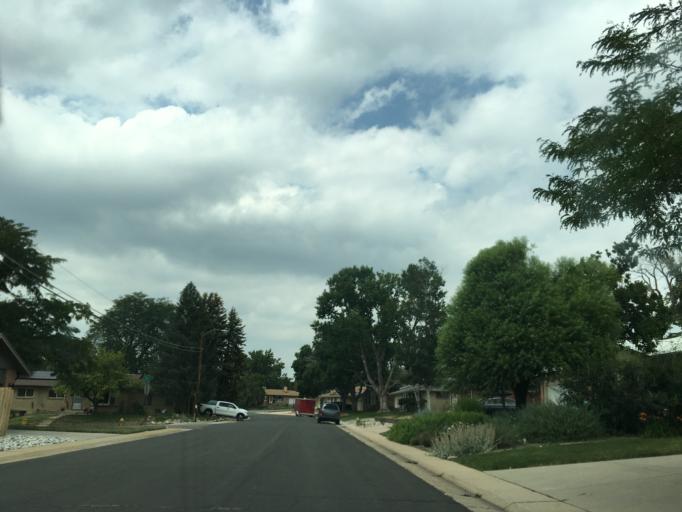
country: US
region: Colorado
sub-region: Arapahoe County
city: Sheridan
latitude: 39.6665
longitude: -105.0391
